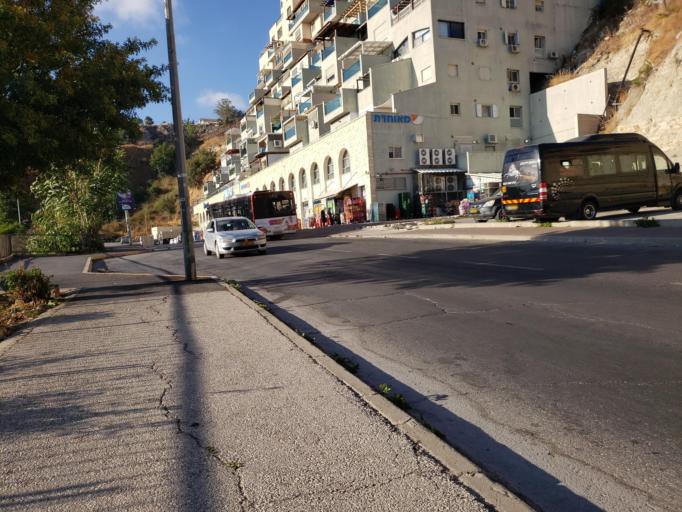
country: IL
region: Northern District
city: Safed
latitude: 32.9640
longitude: 35.4921
